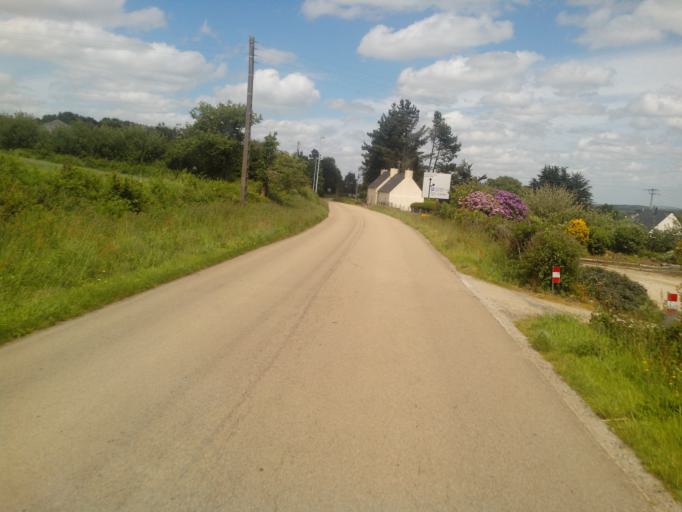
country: FR
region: Brittany
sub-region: Departement du Finistere
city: Guerlesquin
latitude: 48.5131
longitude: -3.6000
